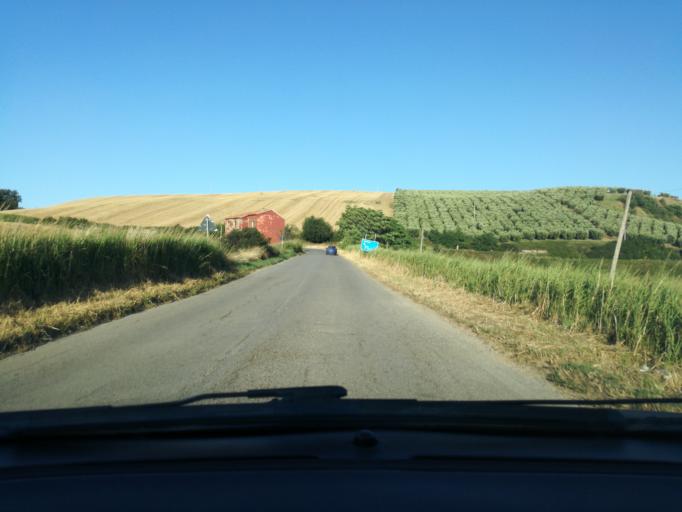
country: IT
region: Molise
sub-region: Provincia di Campobasso
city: Guglionesi
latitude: 41.9331
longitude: 14.9394
